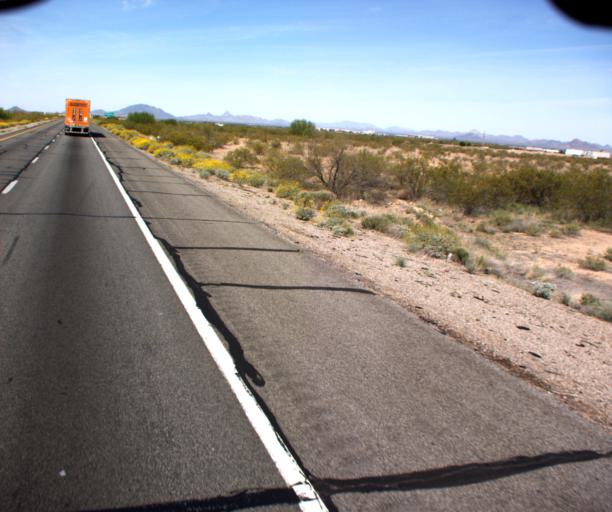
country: US
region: Arizona
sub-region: Maricopa County
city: Buckeye
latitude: 33.4795
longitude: -112.8560
